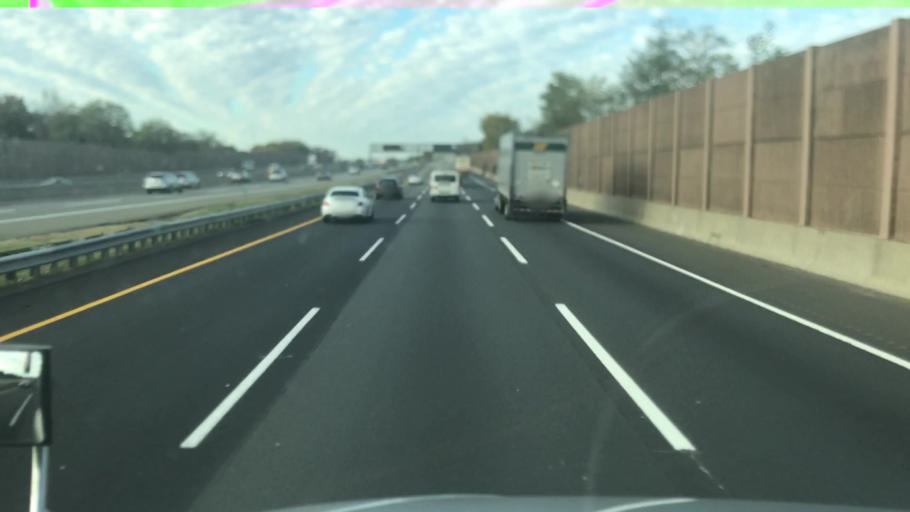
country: US
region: New Jersey
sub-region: Middlesex County
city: Metuchen
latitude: 40.5220
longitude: -74.3523
